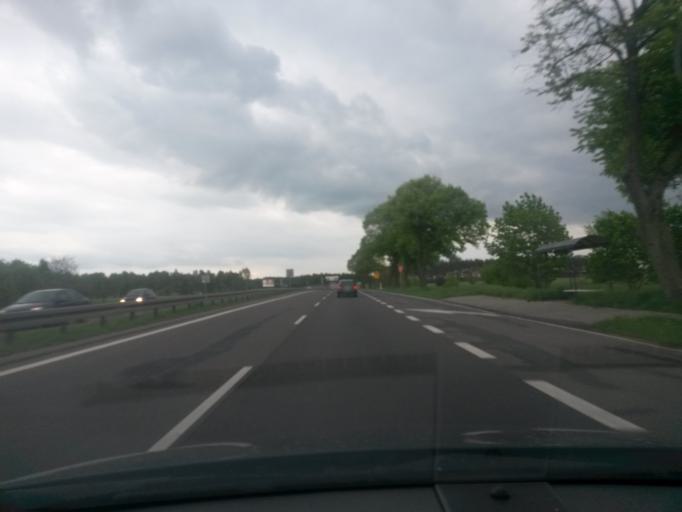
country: PL
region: Masovian Voivodeship
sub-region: Powiat plonski
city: Zaluski
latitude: 52.5801
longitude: 20.4739
